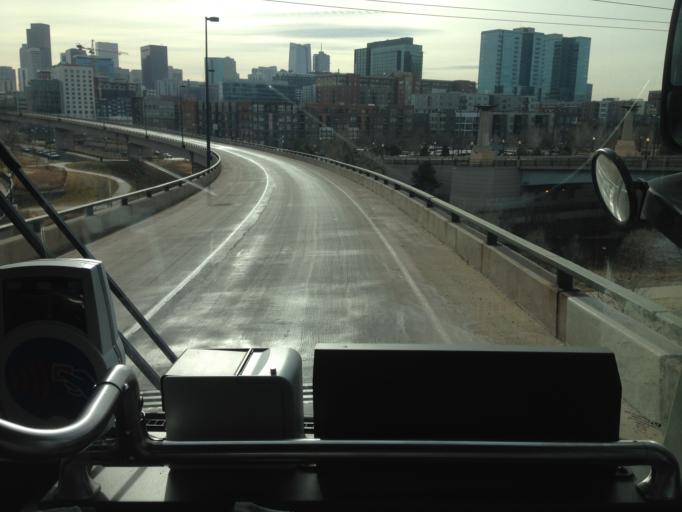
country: US
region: Colorado
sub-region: Denver County
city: Denver
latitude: 39.7615
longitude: -105.0027
